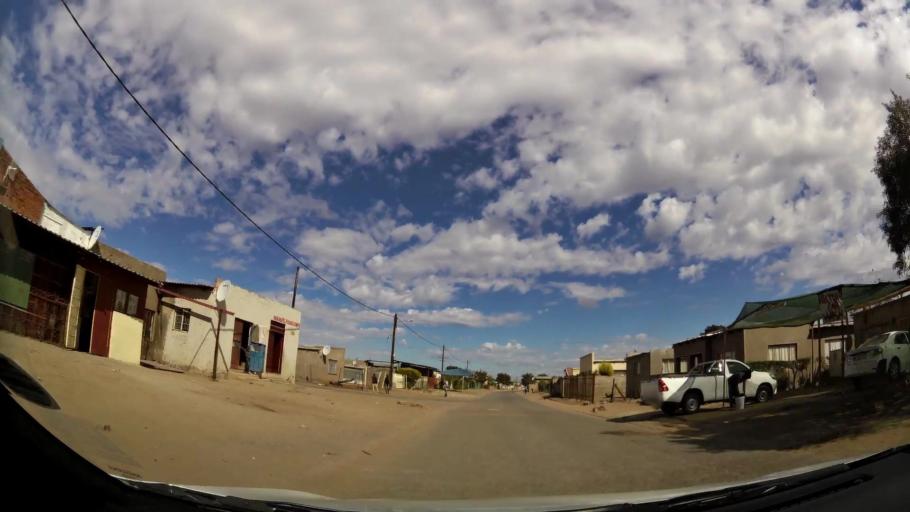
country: ZA
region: Limpopo
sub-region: Waterberg District Municipality
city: Bela-Bela
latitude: -24.8798
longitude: 28.3193
